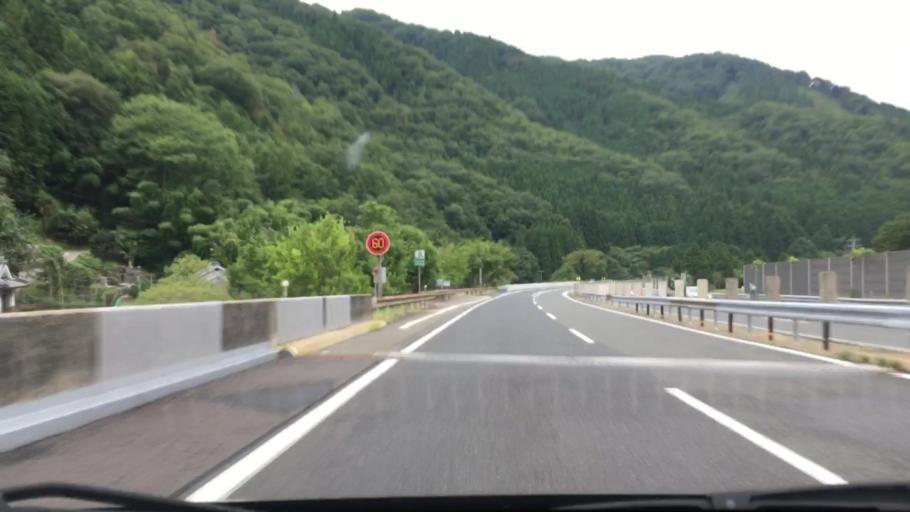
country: JP
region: Okayama
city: Niimi
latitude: 35.0082
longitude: 133.4910
